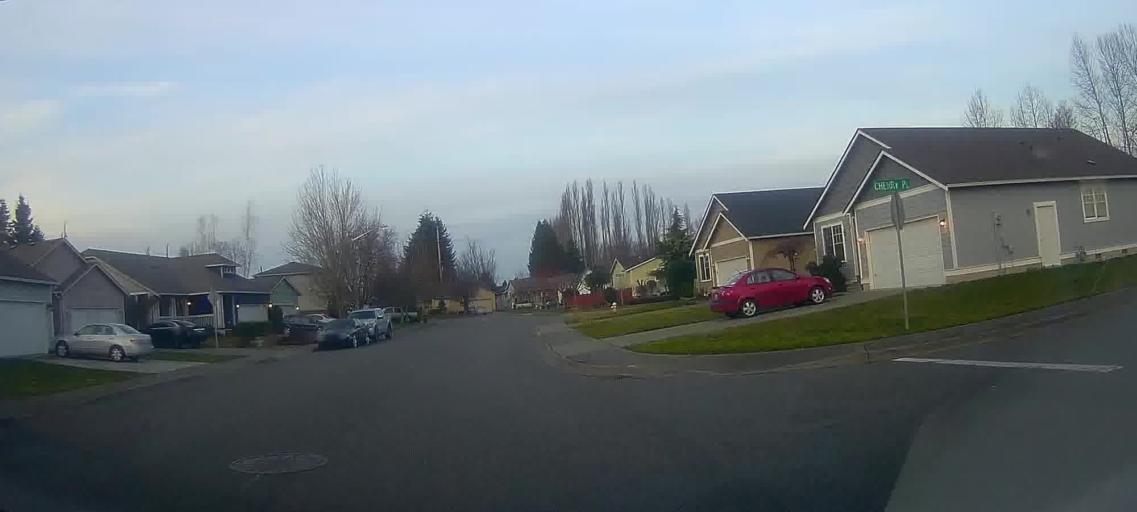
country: US
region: Washington
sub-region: Skagit County
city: Mount Vernon
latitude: 48.4416
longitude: -122.3272
